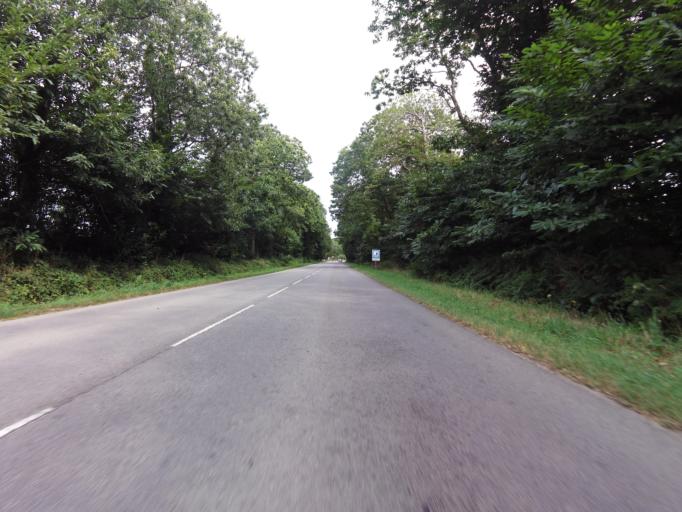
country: FR
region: Brittany
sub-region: Departement du Finistere
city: Poullan-sur-Mer
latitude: 48.0858
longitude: -4.3919
